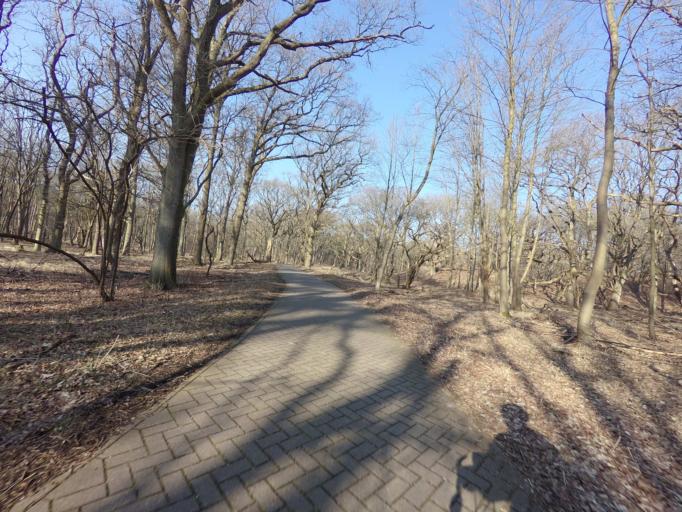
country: NL
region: North Holland
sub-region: Gemeente Bloemendaal
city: Bloemendaal
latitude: 52.4363
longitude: 4.6124
